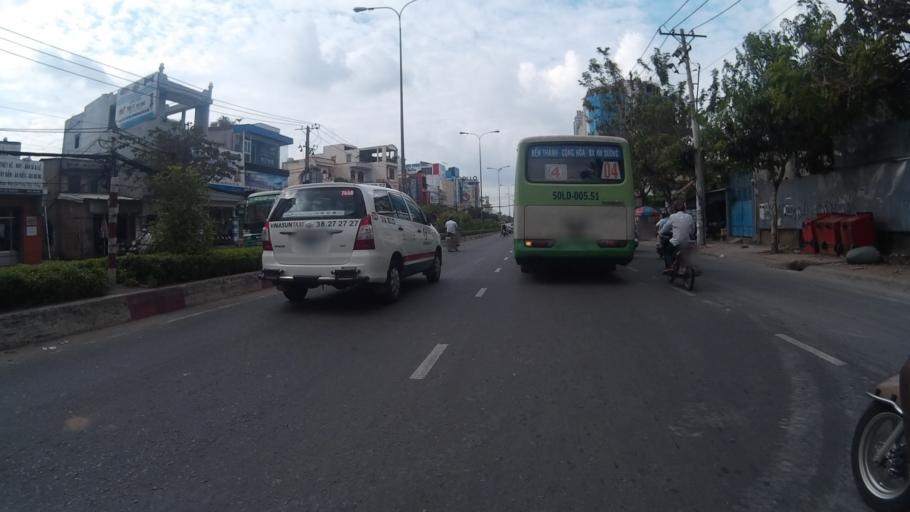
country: VN
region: Ho Chi Minh City
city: Quan Tan Phu
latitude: 10.8034
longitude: 106.6383
